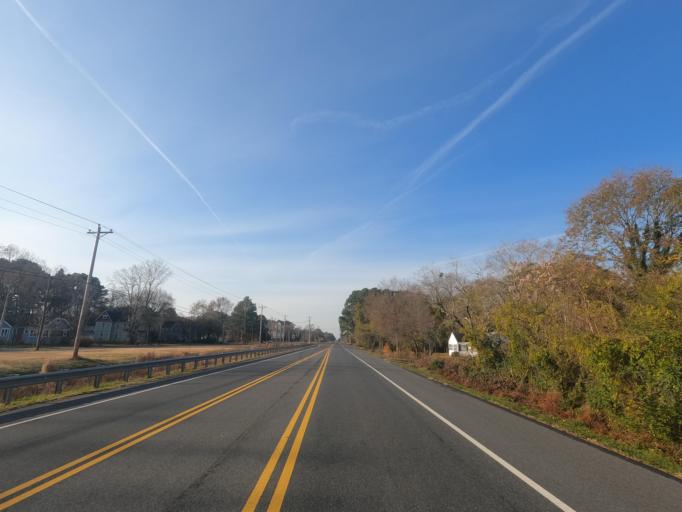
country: US
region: Maryland
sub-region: Somerset County
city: Crisfield
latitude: 38.0382
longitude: -75.7733
